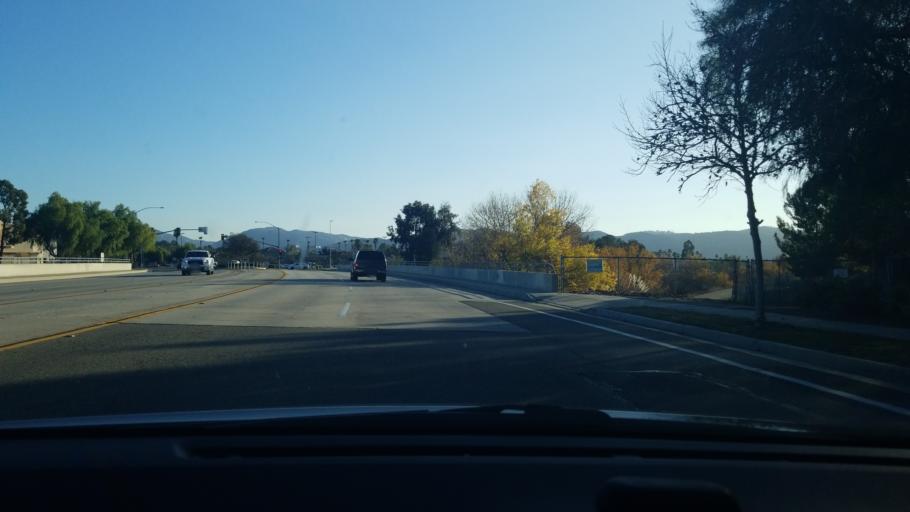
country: US
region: California
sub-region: Riverside County
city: Murrieta Hot Springs
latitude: 33.5339
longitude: -117.1529
